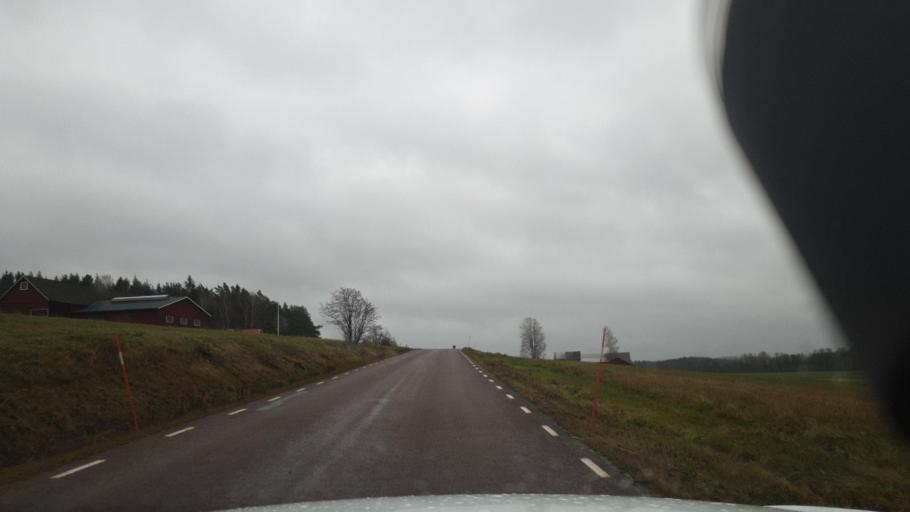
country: SE
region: Vaermland
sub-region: Sunne Kommun
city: Sunne
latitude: 59.7435
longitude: 13.0887
